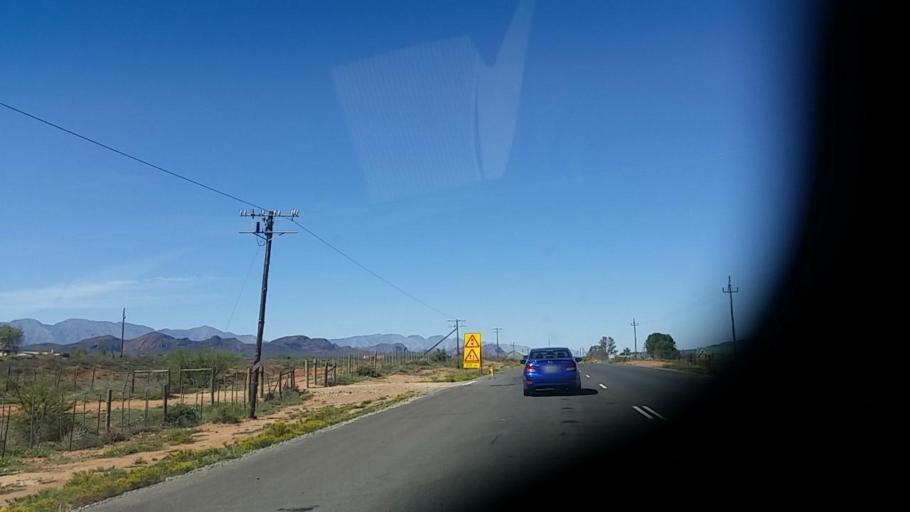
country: ZA
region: Western Cape
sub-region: Eden District Municipality
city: Oudtshoorn
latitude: -33.5820
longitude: 22.3080
